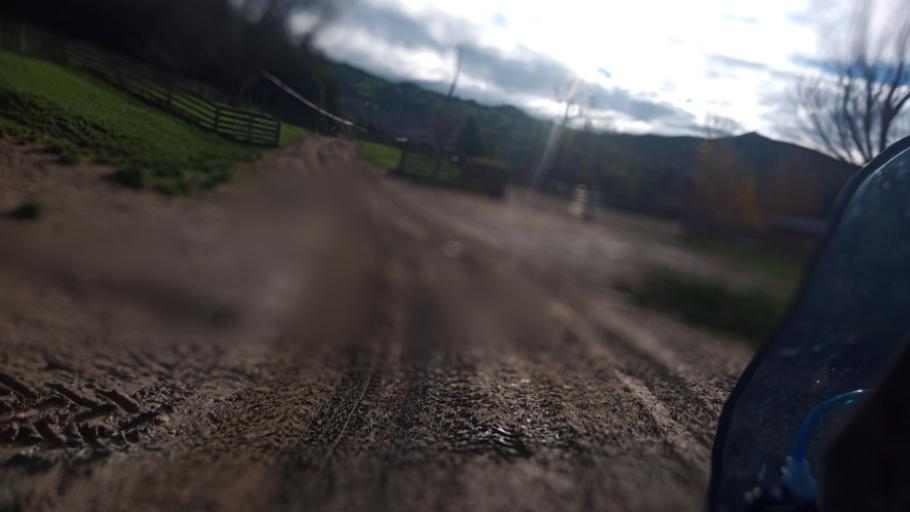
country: NZ
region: Gisborne
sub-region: Gisborne District
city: Gisborne
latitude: -38.3490
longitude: 177.9394
